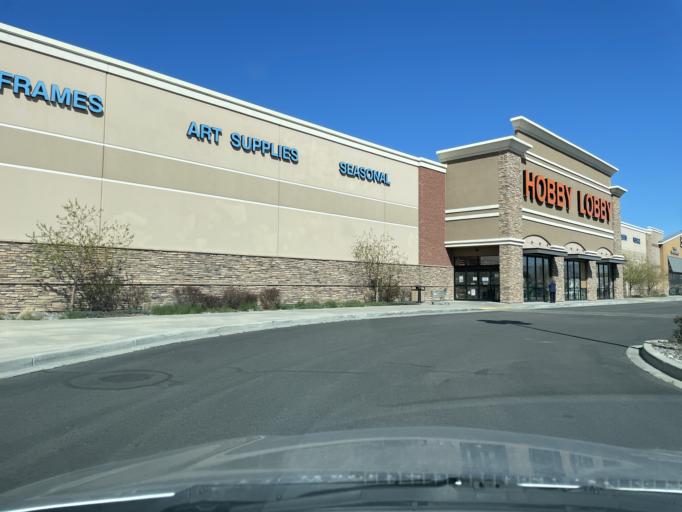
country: US
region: Colorado
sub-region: Mesa County
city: Grand Junction
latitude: 39.0795
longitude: -108.5861
